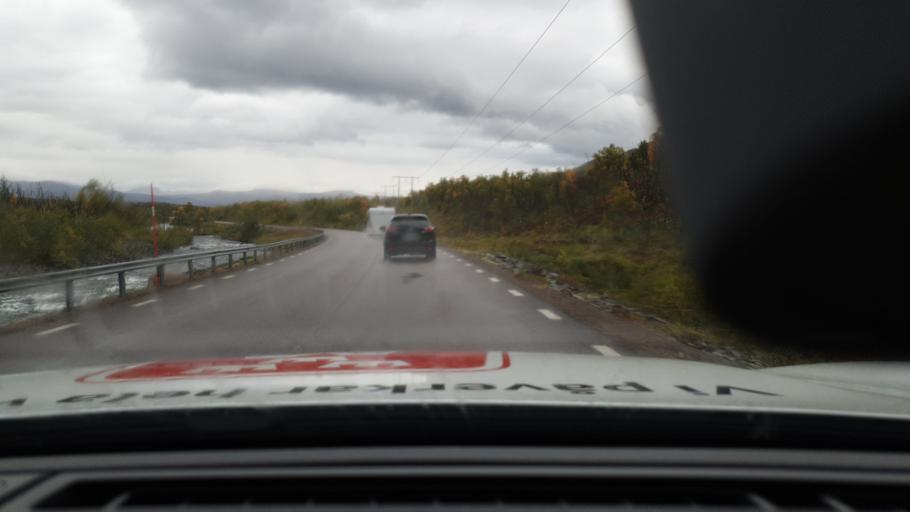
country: NO
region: Troms
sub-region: Bardu
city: Setermoen
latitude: 68.4271
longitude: 18.4380
